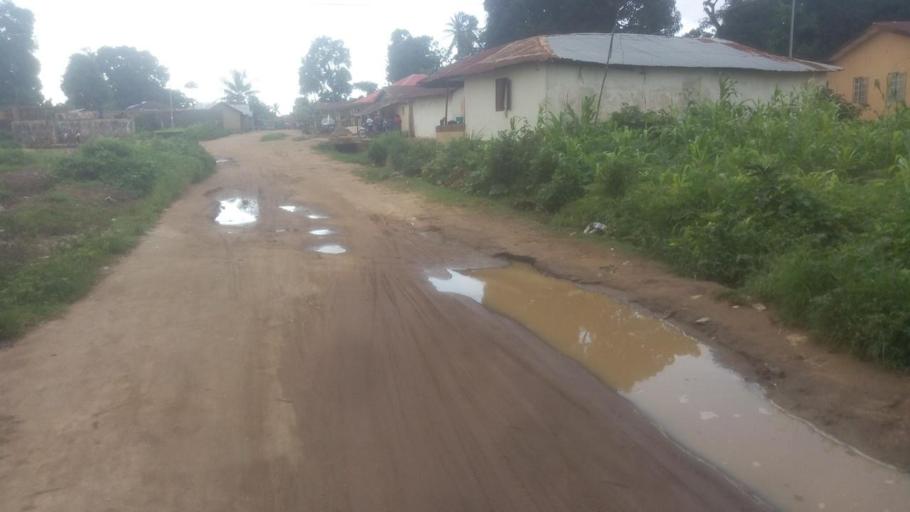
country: SL
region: Northern Province
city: Masoyila
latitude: 8.6090
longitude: -13.1891
